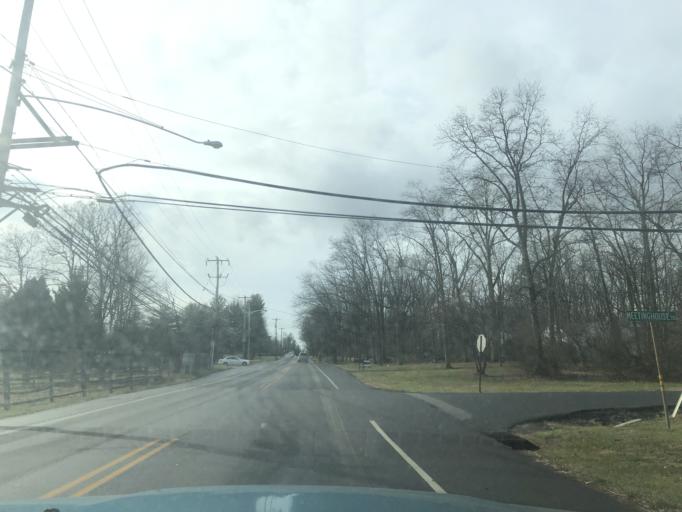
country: US
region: Pennsylvania
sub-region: Montgomery County
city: Harleysville
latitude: 40.2709
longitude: -75.3972
